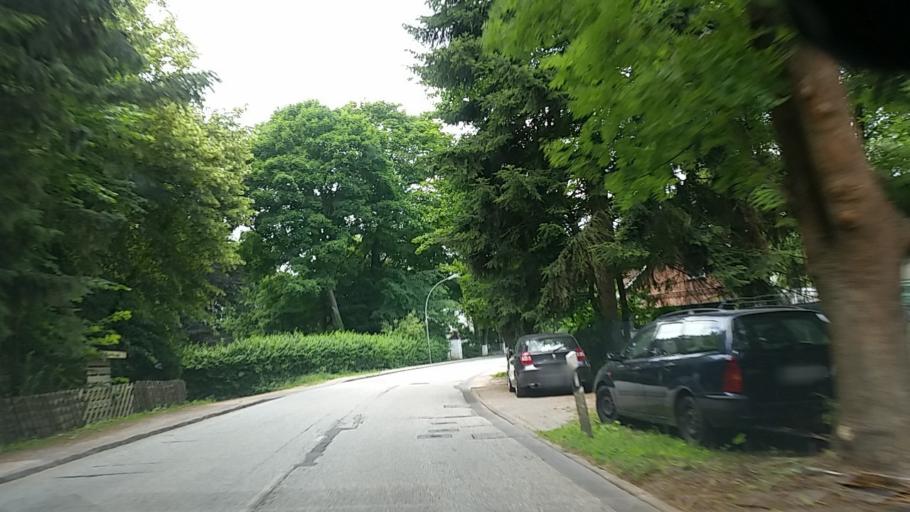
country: DE
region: Hamburg
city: Wandsbek
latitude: 53.5244
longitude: 10.1111
